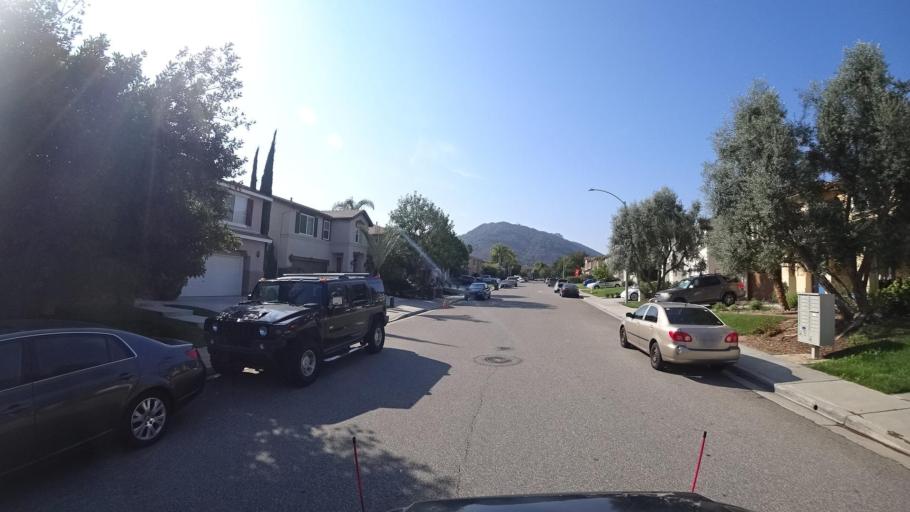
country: US
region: California
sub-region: San Diego County
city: Bonsall
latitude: 33.3209
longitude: -117.1481
